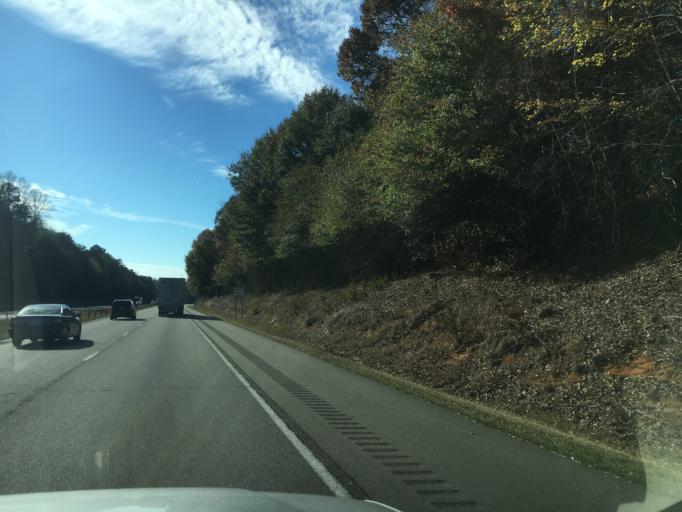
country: US
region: North Carolina
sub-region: Catawba County
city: Claremont
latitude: 35.7482
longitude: -81.0614
